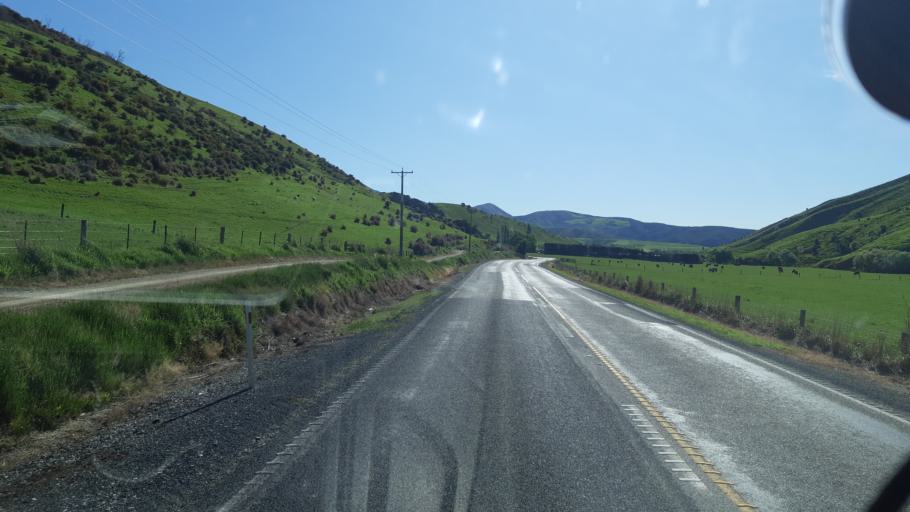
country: NZ
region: Otago
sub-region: Clutha District
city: Balclutha
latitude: -45.8292
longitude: 169.5530
